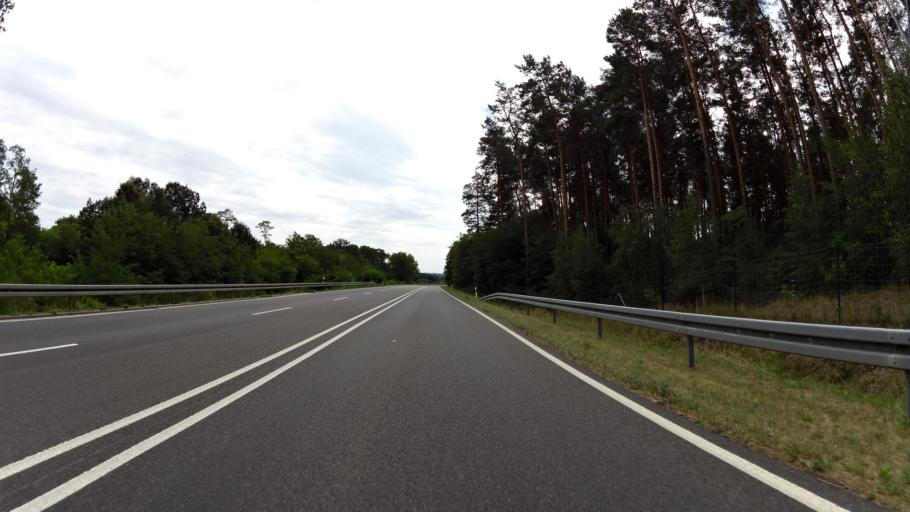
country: DE
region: Brandenburg
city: Guben
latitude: 52.0183
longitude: 14.6796
